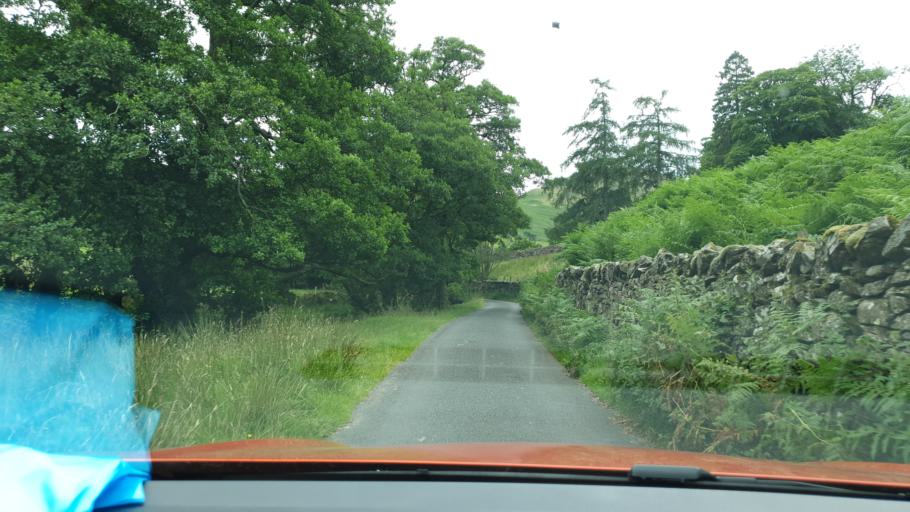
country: GB
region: England
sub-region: Cumbria
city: Ambleside
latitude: 54.5645
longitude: -2.8891
